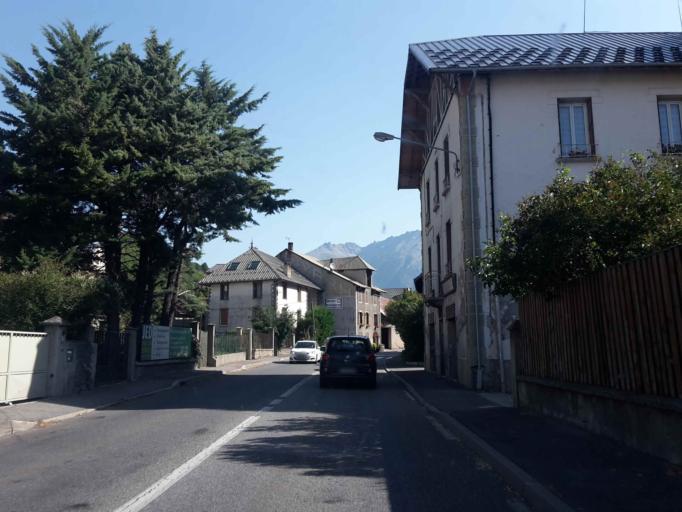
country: FR
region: Provence-Alpes-Cote d'Azur
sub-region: Departement des Hautes-Alpes
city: Guillestre
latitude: 44.6481
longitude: 6.5782
